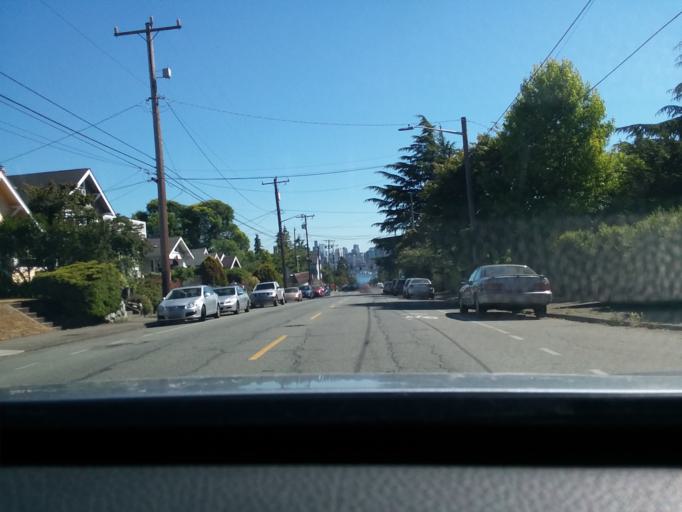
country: US
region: Washington
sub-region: King County
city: Seattle
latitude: 47.6569
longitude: -122.3363
